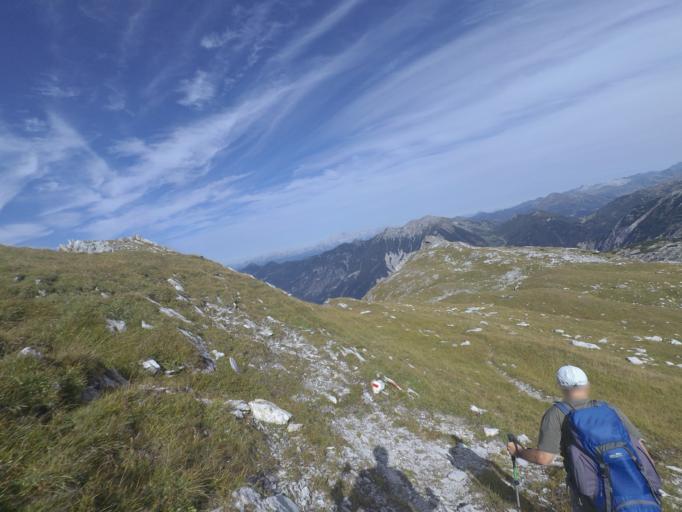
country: AT
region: Salzburg
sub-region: Politischer Bezirk Sankt Johann im Pongau
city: Kleinarl
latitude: 47.2270
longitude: 13.3915
